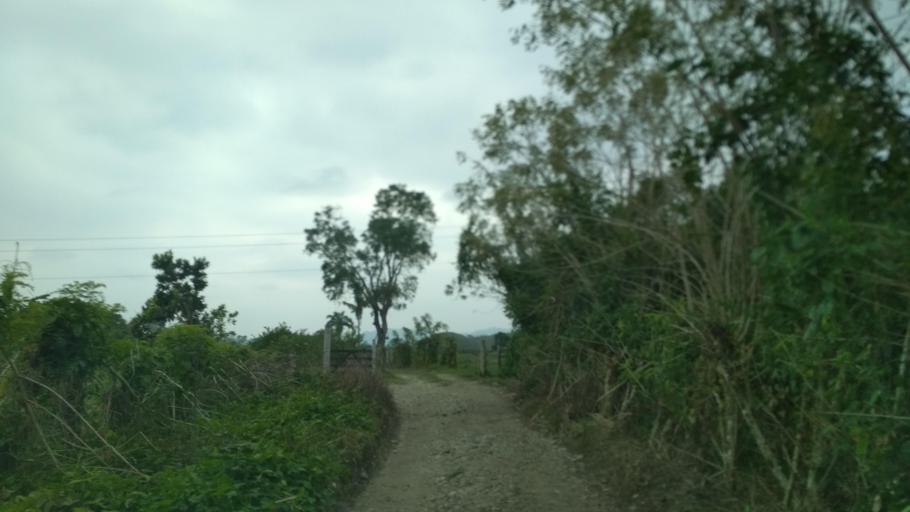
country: MM
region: Kayah
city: Loikaw
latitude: 20.2113
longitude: 97.3319
